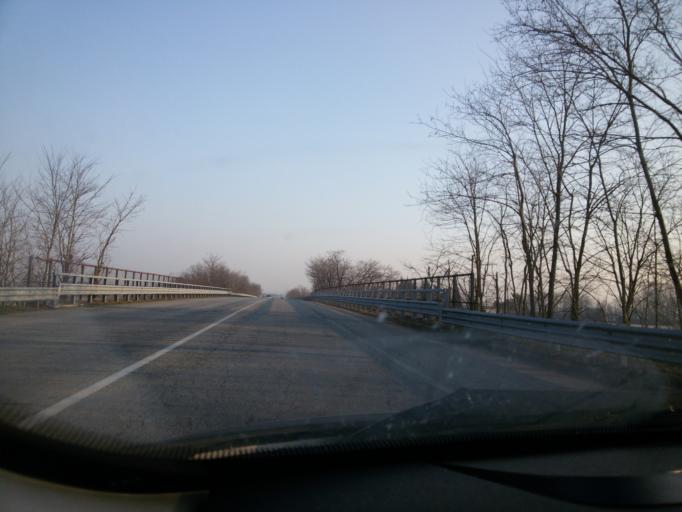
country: IT
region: Piedmont
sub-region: Provincia di Vercelli
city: Stroppiana
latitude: 45.2473
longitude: 8.4595
